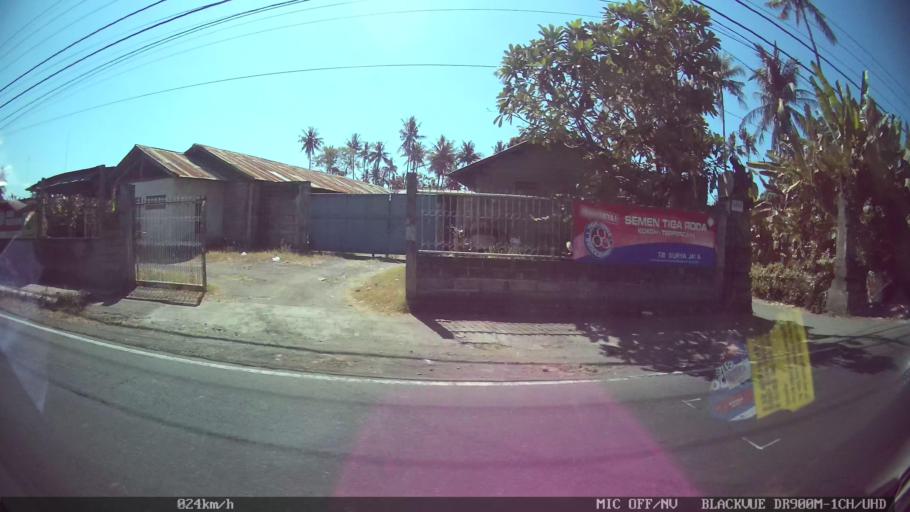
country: ID
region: Bali
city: Banjar Banyualit
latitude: -8.1540
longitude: 115.0391
